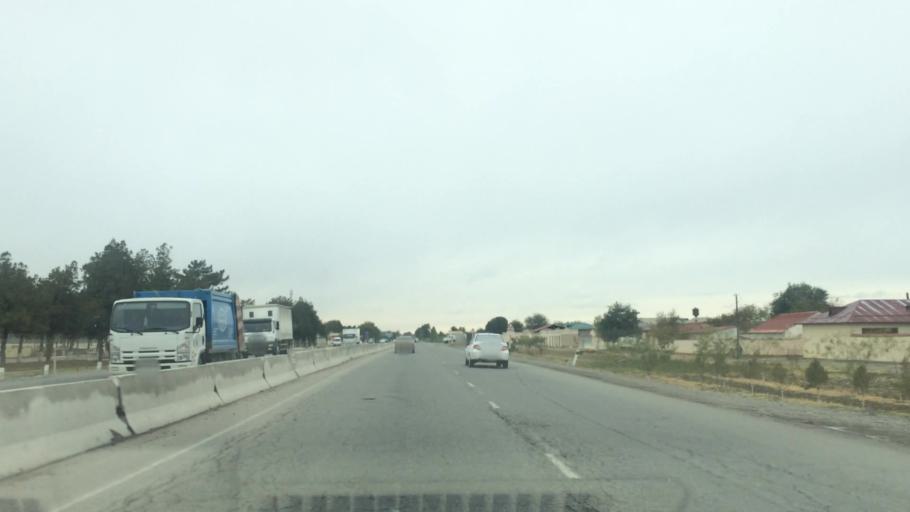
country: UZ
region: Samarqand
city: Jomboy
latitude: 39.7256
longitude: 67.1379
